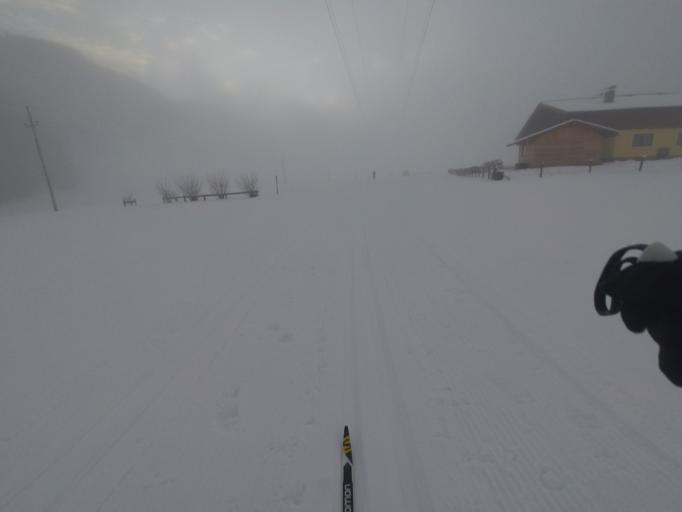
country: AT
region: Salzburg
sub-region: Politischer Bezirk Sankt Johann im Pongau
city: Wagrain
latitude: 47.3562
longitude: 13.3379
